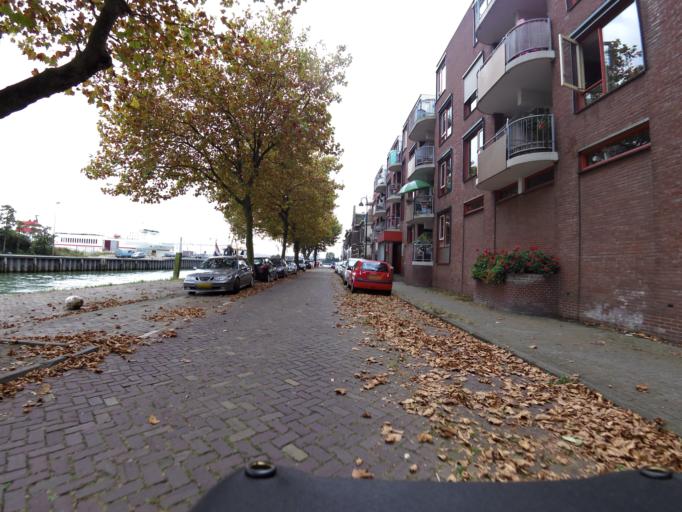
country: NL
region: South Holland
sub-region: Gemeente Vlaardingen
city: Vlaardingen
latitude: 51.9008
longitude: 4.3479
